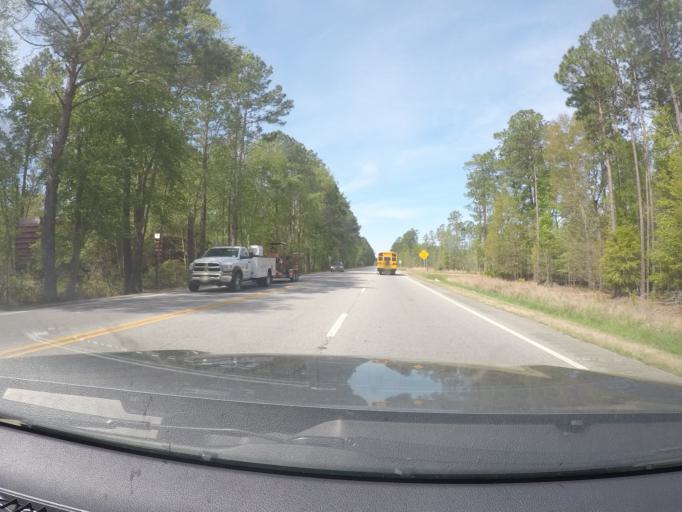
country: US
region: Georgia
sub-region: Bryan County
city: Pembroke
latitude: 32.1302
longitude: -81.5427
